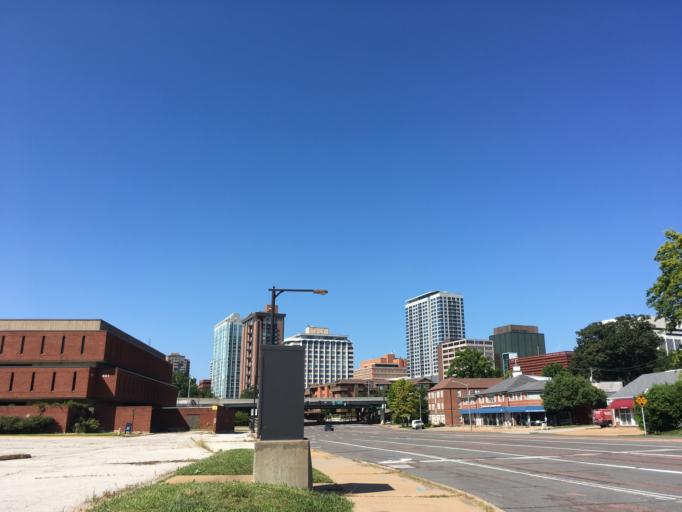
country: US
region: Missouri
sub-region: Saint Louis County
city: Clayton
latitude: 38.6439
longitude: -90.3433
